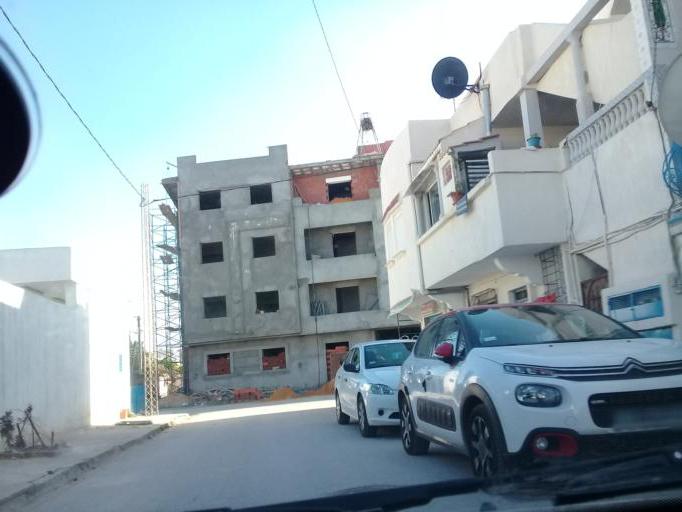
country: TN
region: Tunis
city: La Goulette
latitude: 36.8242
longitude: 10.3085
